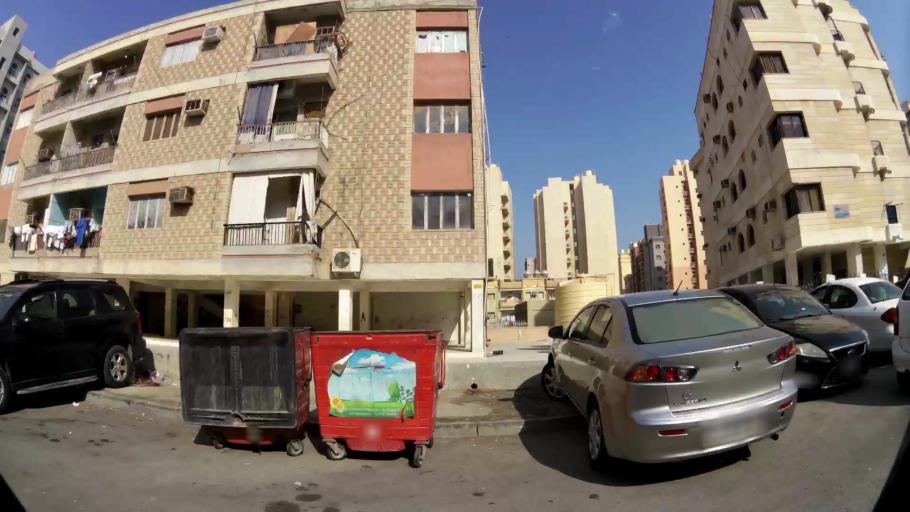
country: KW
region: Muhafazat Hawalli
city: Hawalli
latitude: 29.3307
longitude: 48.0199
